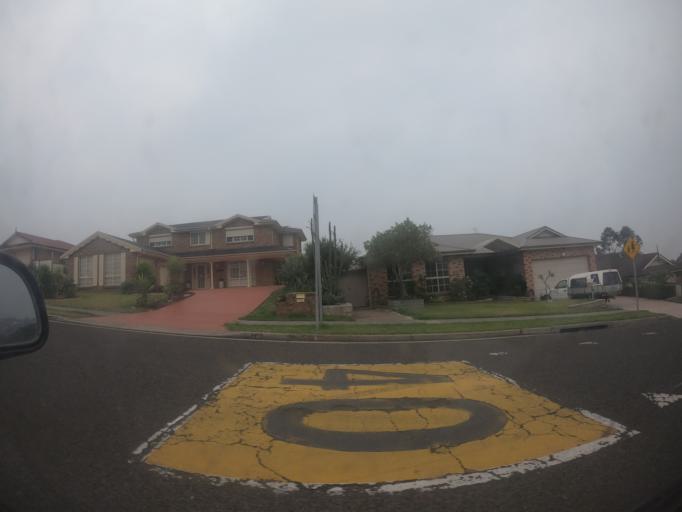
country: AU
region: New South Wales
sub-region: Shellharbour
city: Flinders
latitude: -34.5811
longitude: 150.8470
